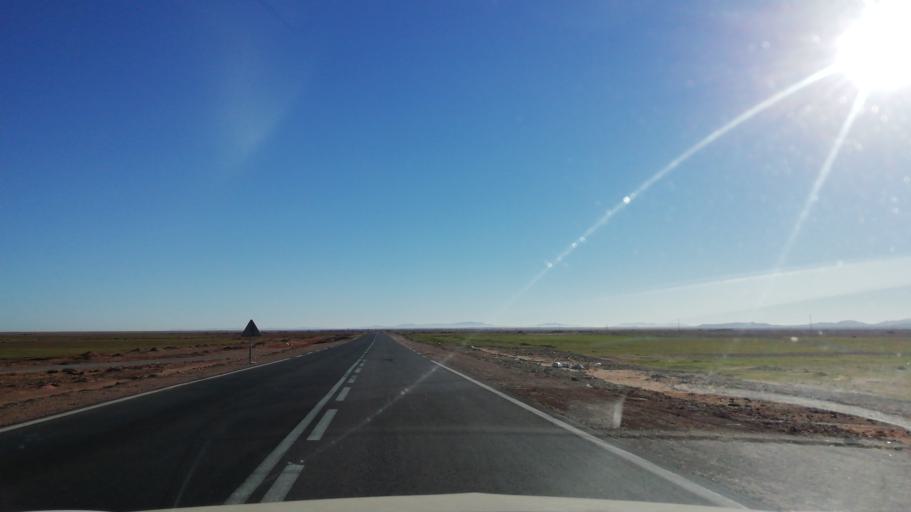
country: DZ
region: El Bayadh
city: El Bayadh
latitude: 33.8590
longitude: 0.5670
